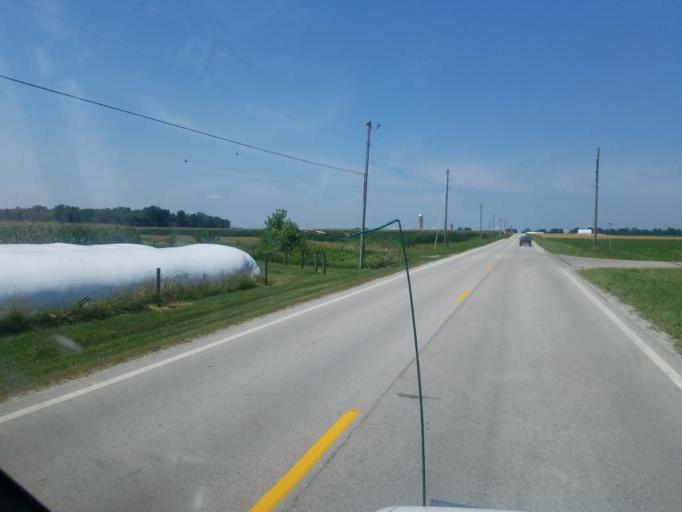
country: US
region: Ohio
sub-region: Auglaize County
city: Minster
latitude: 40.3742
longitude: -84.4340
